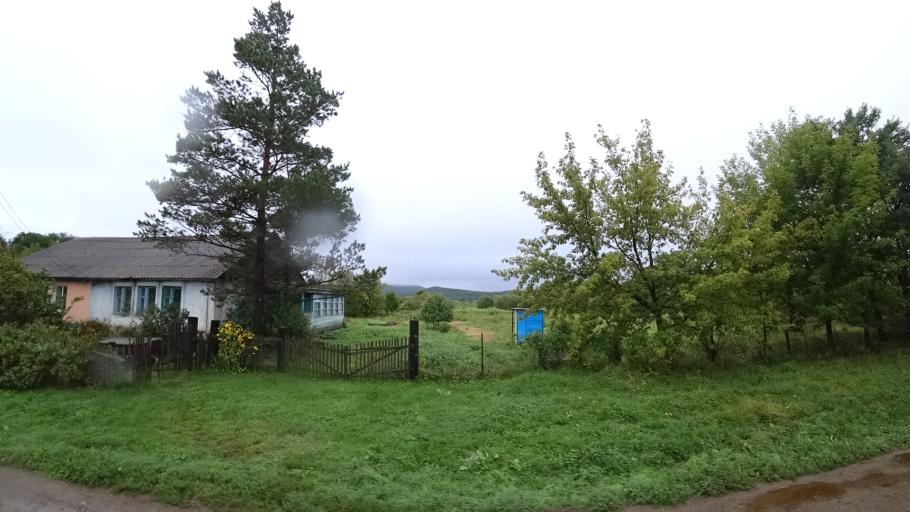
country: RU
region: Primorskiy
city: Monastyrishche
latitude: 44.2570
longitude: 132.4276
